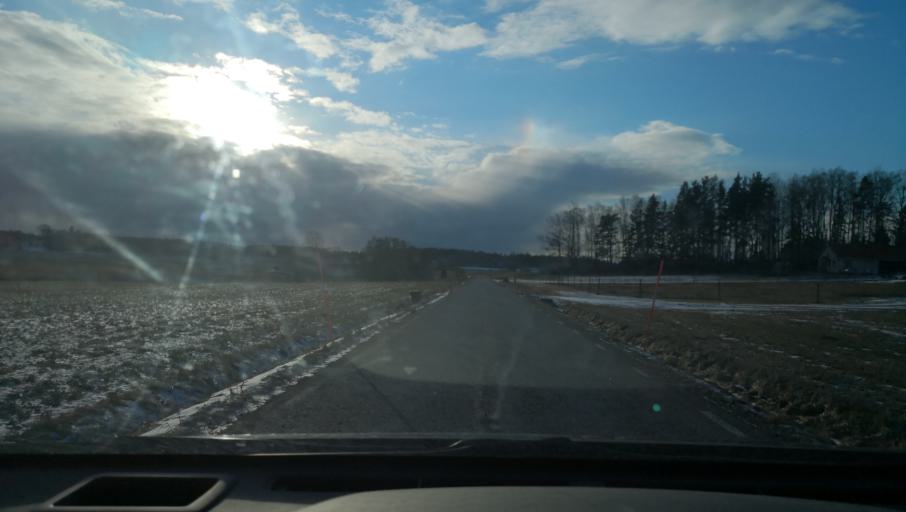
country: SE
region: Uppsala
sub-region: Enkopings Kommun
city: Irsta
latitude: 59.6603
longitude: 16.8129
